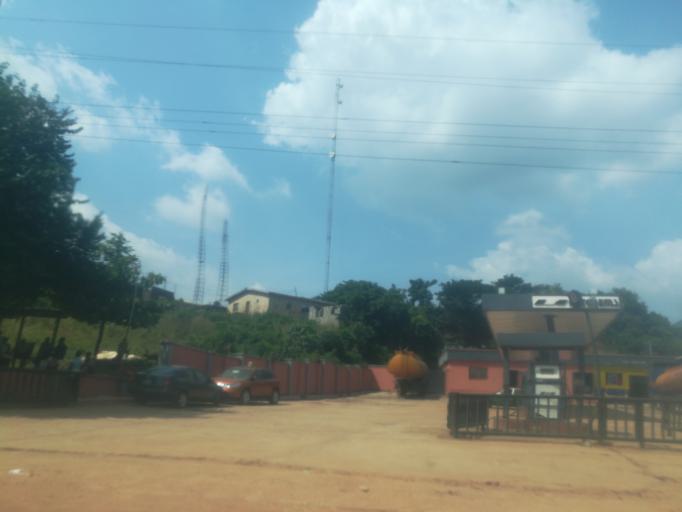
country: NG
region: Ogun
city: Abeokuta
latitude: 7.1757
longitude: 3.3845
